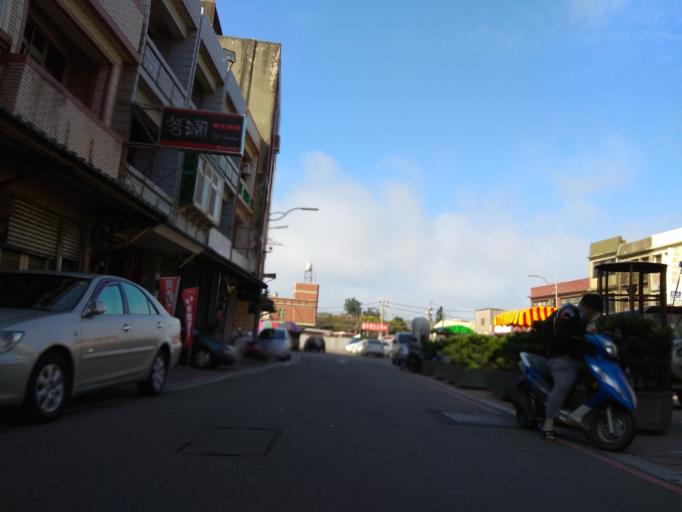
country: TW
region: Taiwan
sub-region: Hsinchu
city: Zhubei
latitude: 25.0371
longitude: 121.0815
